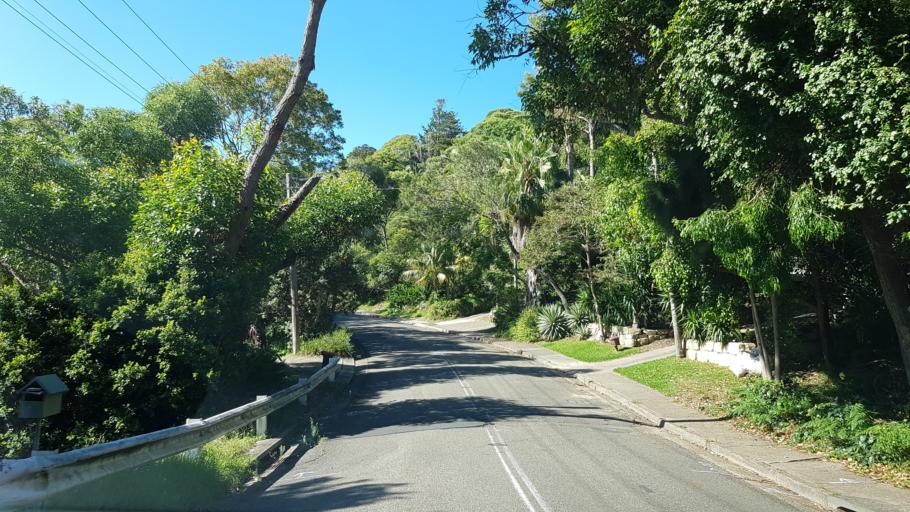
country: AU
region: New South Wales
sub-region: Pittwater
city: Bilgola Beach
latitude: -33.6211
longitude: 151.3382
